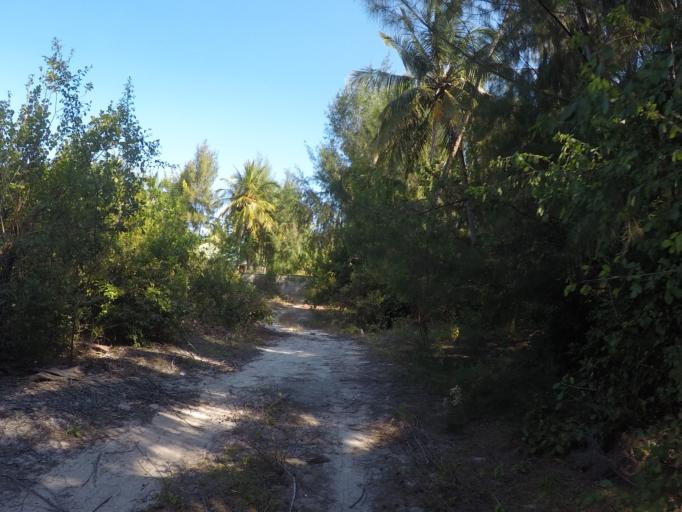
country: TZ
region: Zanzibar Central/South
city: Nganane
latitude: -6.2789
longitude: 39.5355
